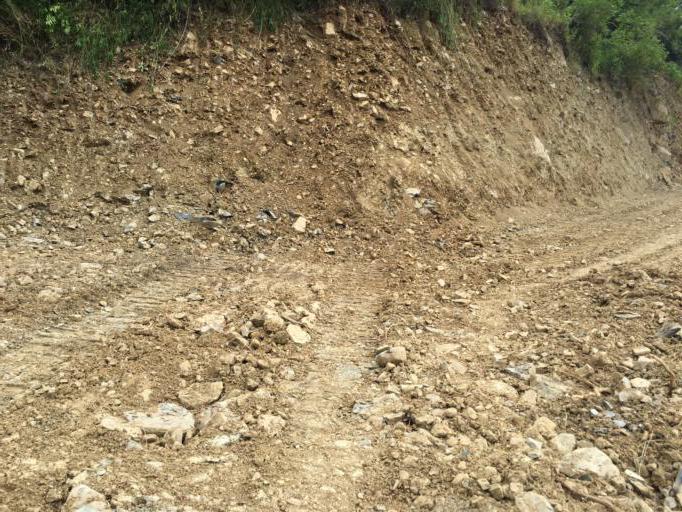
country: CN
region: Guangxi Zhuangzu Zizhiqu
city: Tongle
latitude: 25.1232
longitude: 106.4227
